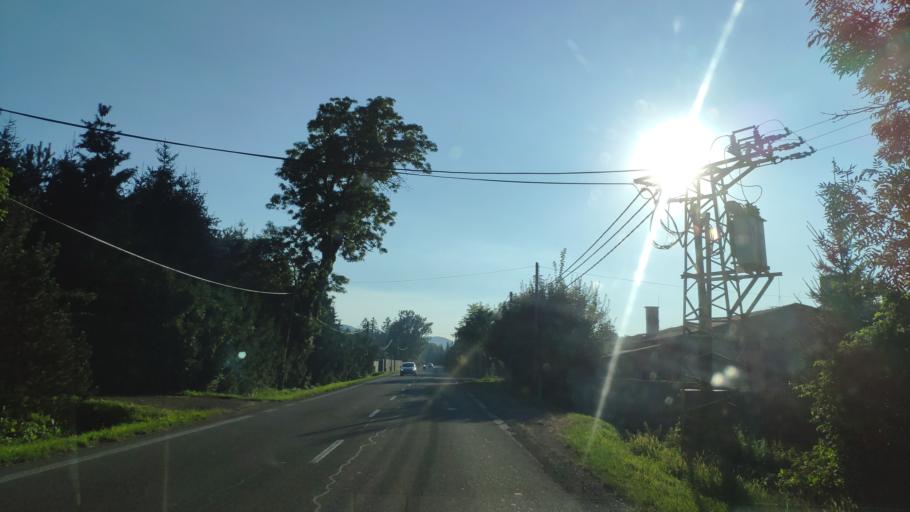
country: SK
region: Presovsky
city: Chlmec
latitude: 48.9367
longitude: 22.0069
